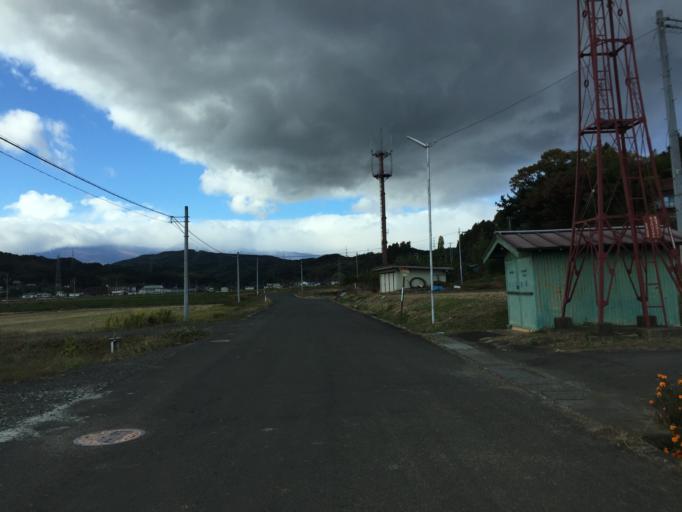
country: JP
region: Fukushima
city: Nihommatsu
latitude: 37.6630
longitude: 140.4314
